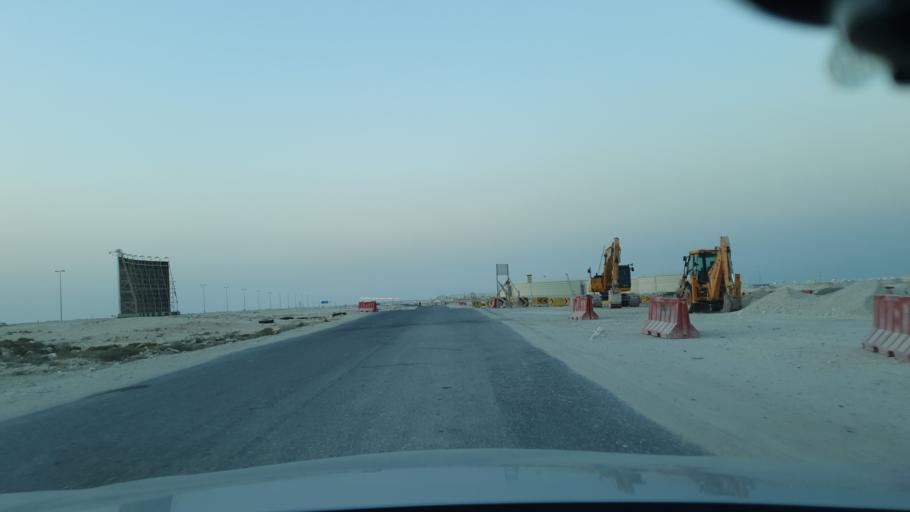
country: BH
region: Central Governorate
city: Dar Kulayb
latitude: 25.9714
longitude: 50.6020
